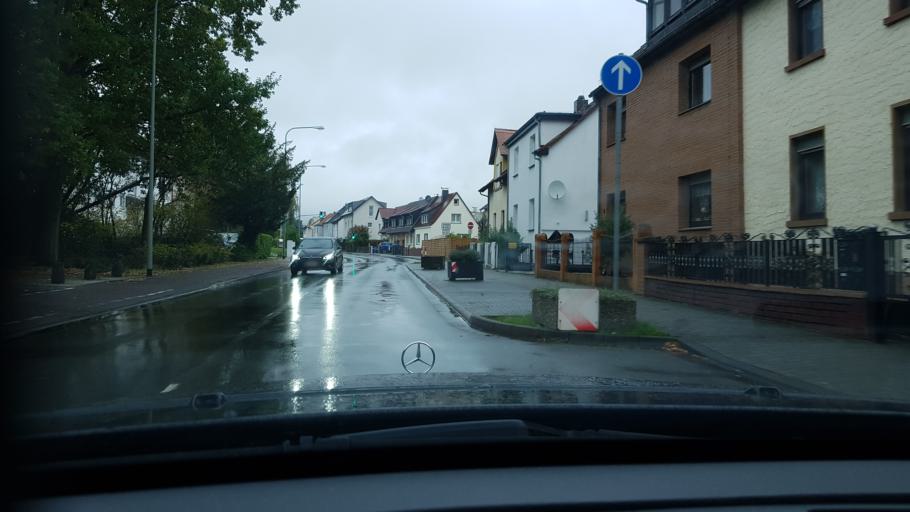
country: DE
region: Hesse
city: Schwalbach am Taunus
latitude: 50.1448
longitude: 8.5326
